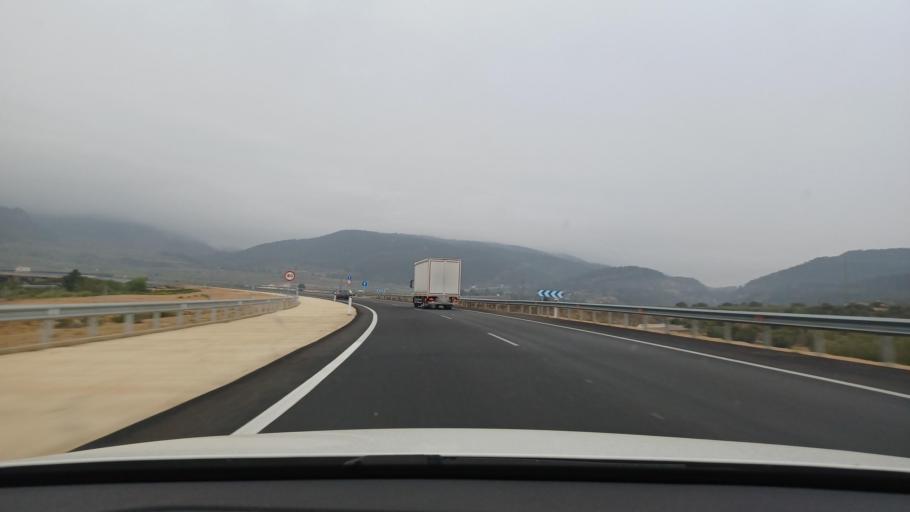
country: ES
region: Valencia
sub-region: Provincia de Valencia
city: La Font de la Figuera
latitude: 38.8302
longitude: -0.8906
